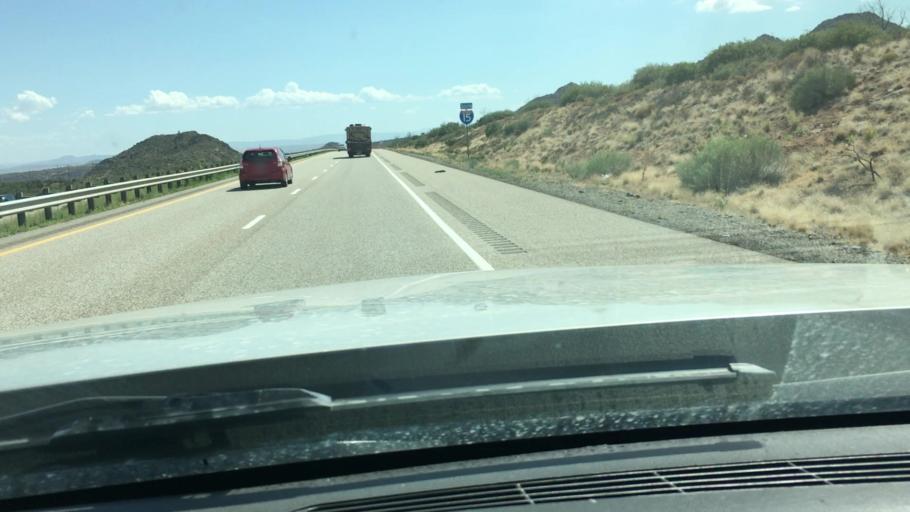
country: US
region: Utah
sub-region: Washington County
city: Toquerville
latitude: 37.3196
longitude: -113.2901
